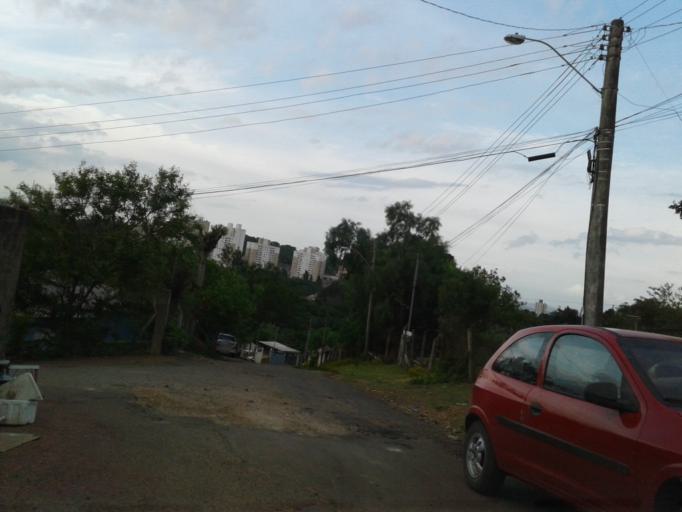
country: BR
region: Rio Grande do Sul
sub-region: Porto Alegre
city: Porto Alegre
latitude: -30.0548
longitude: -51.1403
